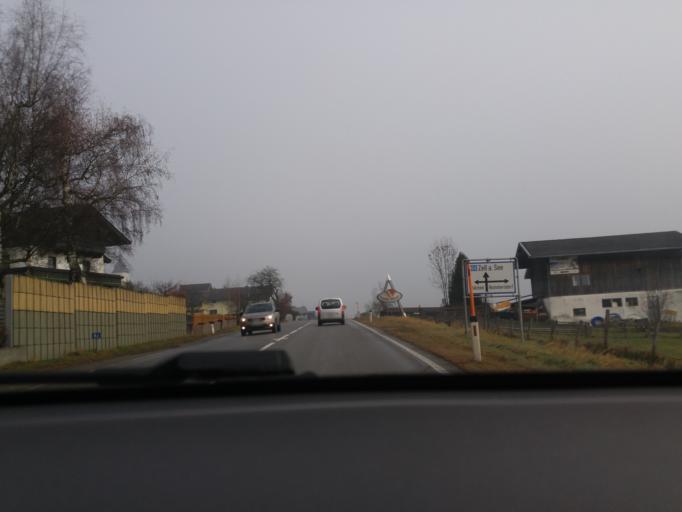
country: AT
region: Salzburg
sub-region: Politischer Bezirk Zell am See
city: Piesendorf
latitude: 47.2881
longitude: 12.6894
